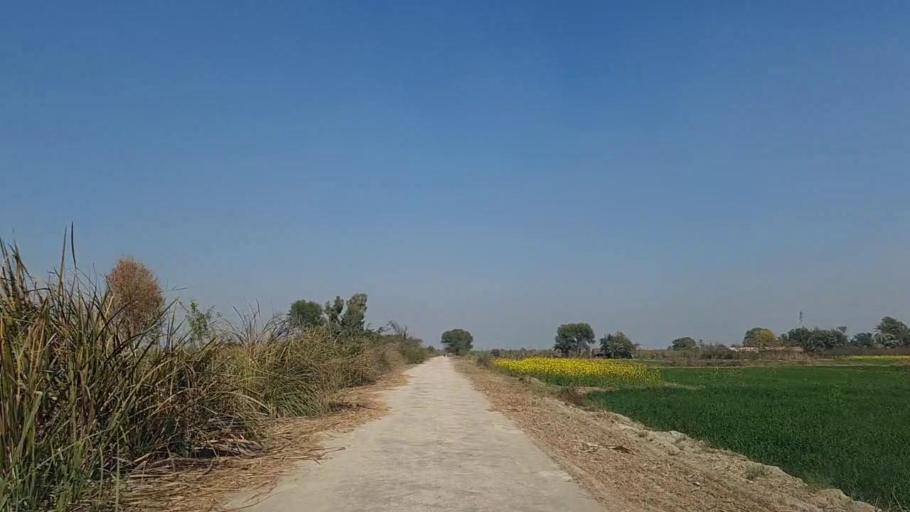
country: PK
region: Sindh
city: Daur
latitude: 26.5005
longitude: 68.3463
